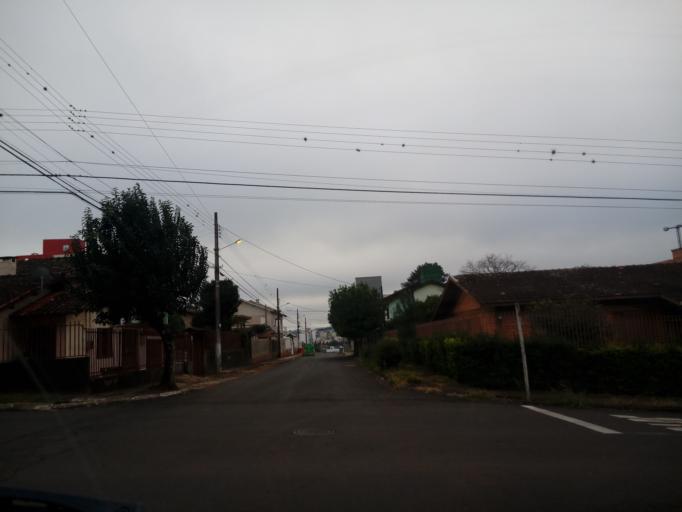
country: BR
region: Santa Catarina
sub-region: Chapeco
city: Chapeco
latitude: -27.0908
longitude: -52.6287
